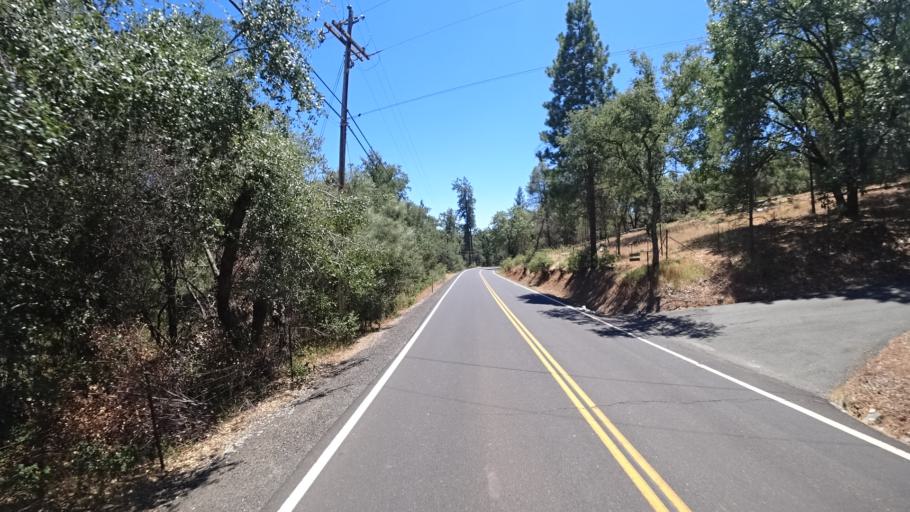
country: US
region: California
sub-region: Calaveras County
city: Mountain Ranch
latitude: 38.2474
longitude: -120.5183
